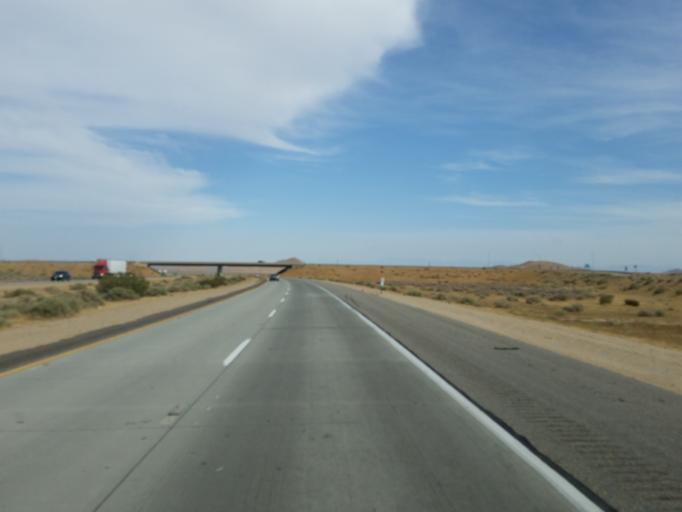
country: US
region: California
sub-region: Kern County
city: Mojave
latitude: 35.0412
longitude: -118.1099
